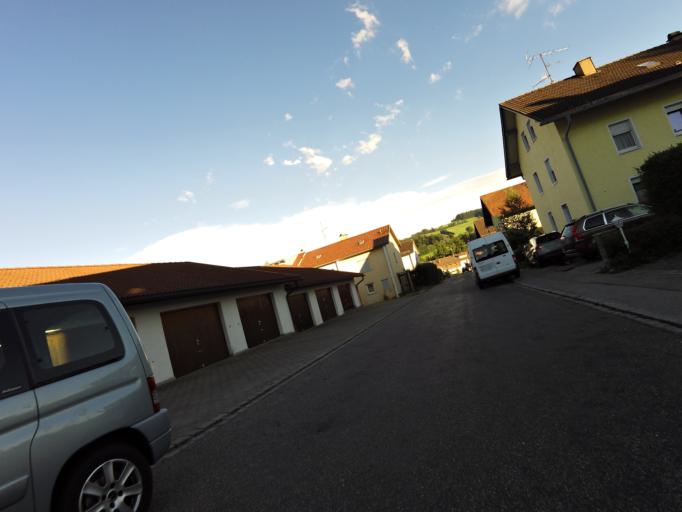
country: DE
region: Bavaria
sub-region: Swabia
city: Weiler-Simmerberg
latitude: 47.5793
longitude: 9.9025
